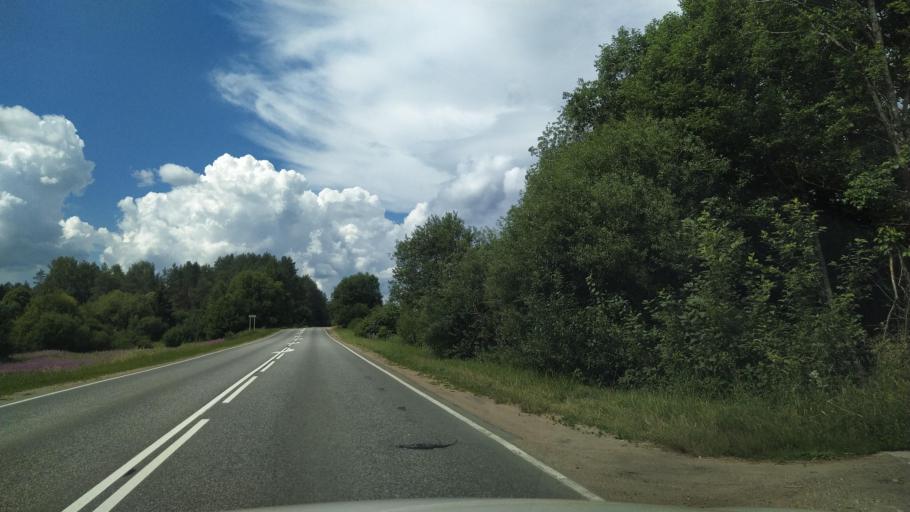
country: RU
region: Leningrad
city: Rozhdestveno
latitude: 59.3446
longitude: 29.9451
